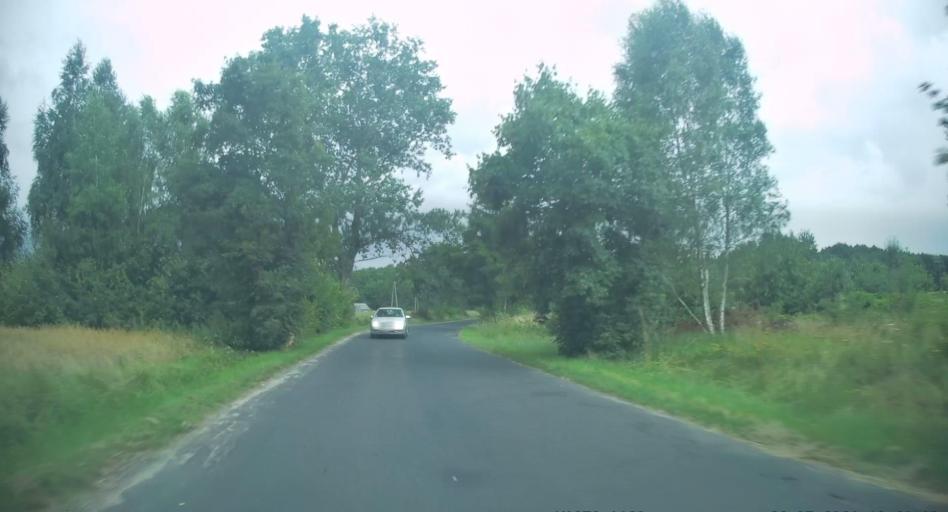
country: PL
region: Lodz Voivodeship
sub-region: Powiat rawski
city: Rawa Mazowiecka
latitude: 51.7417
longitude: 20.1888
